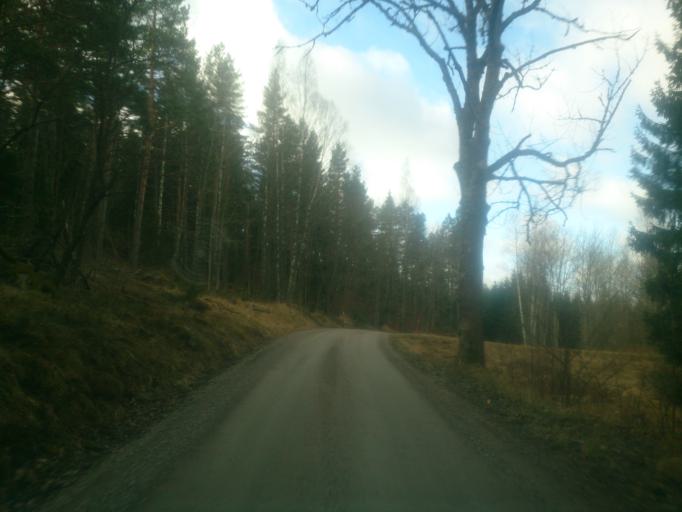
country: SE
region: OEstergoetland
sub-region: Atvidabergs Kommun
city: Atvidaberg
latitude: 58.2014
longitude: 16.1555
